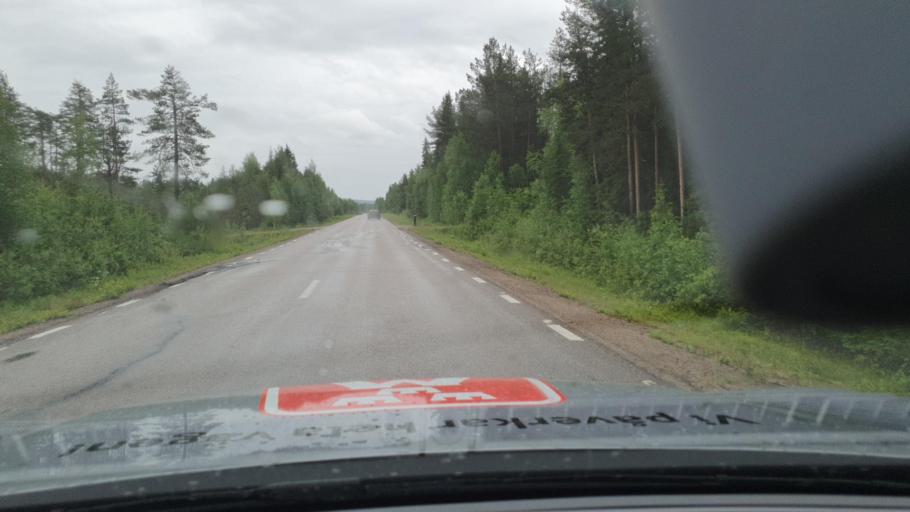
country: SE
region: Norrbotten
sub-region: Overkalix Kommun
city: OEverkalix
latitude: 66.6359
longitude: 22.7271
